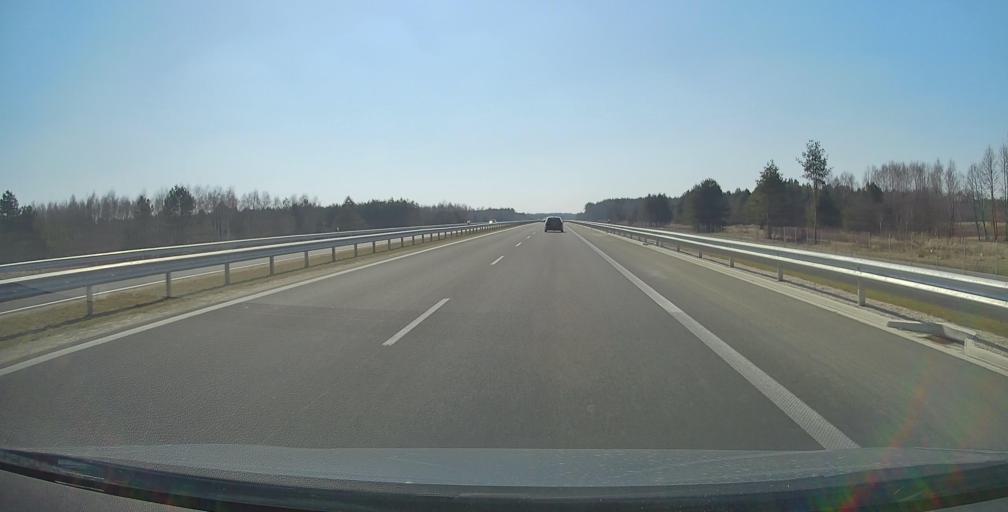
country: PL
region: Subcarpathian Voivodeship
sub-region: Powiat nizanski
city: Konczyce
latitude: 50.4516
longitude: 22.1409
